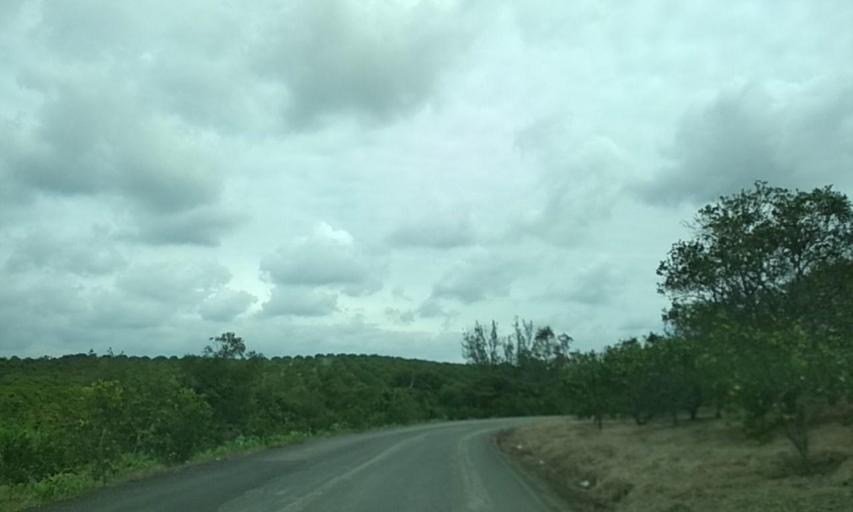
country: MX
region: Veracruz
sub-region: Papantla
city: El Chote
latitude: 20.3547
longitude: -97.3594
